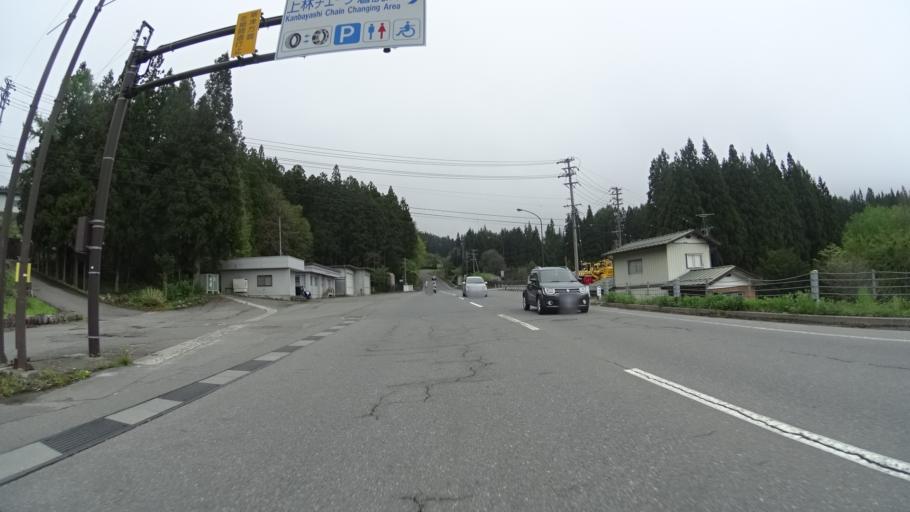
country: JP
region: Nagano
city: Nakano
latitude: 36.7242
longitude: 138.4451
